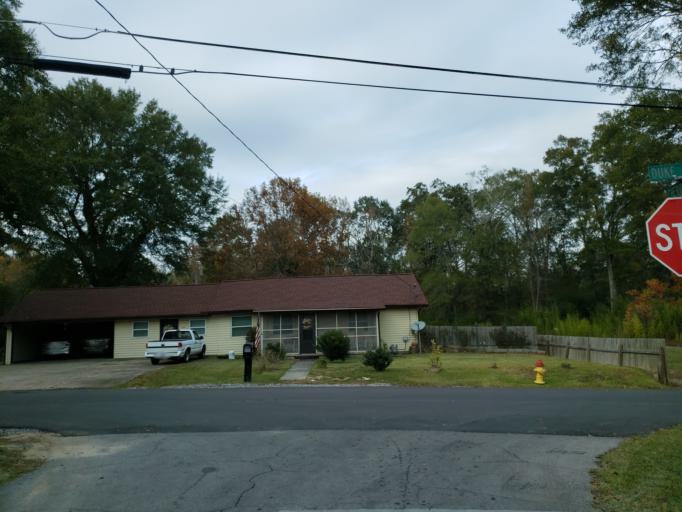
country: US
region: Mississippi
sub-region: Forrest County
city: Hattiesburg
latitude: 31.3118
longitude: -89.2894
